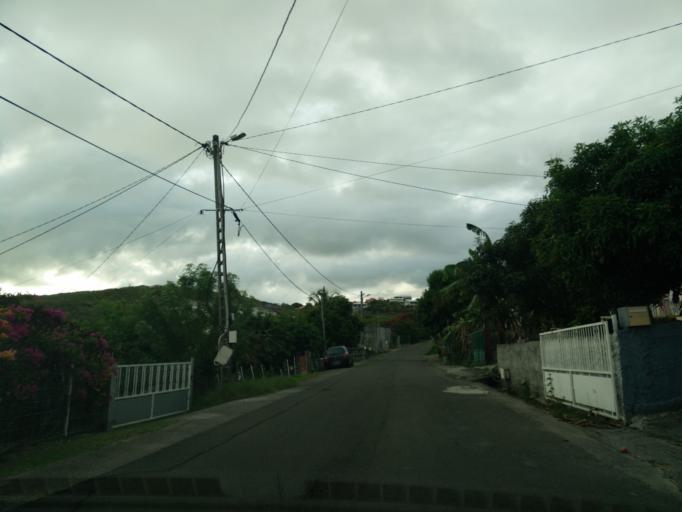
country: MQ
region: Martinique
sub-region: Martinique
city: Le Marin
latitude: 14.4428
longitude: -60.8349
